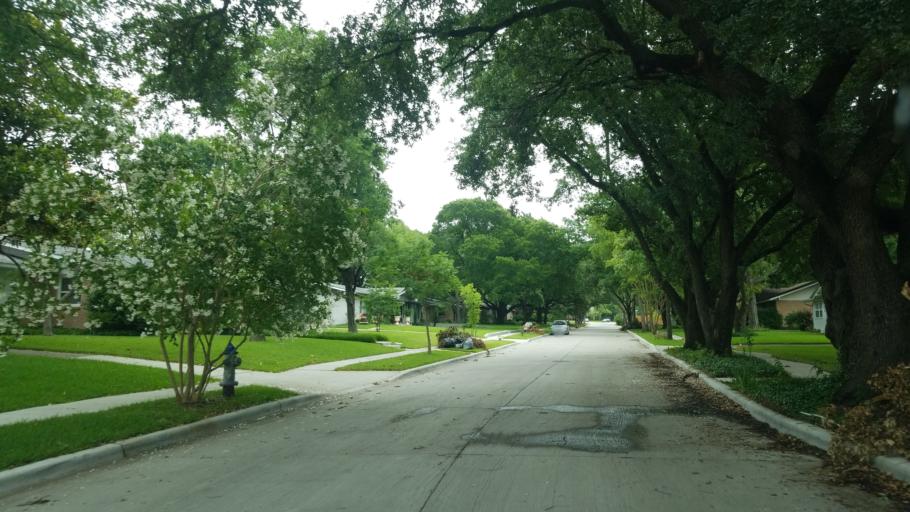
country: US
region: Texas
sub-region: Dallas County
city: Farmers Branch
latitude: 32.9076
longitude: -96.8586
